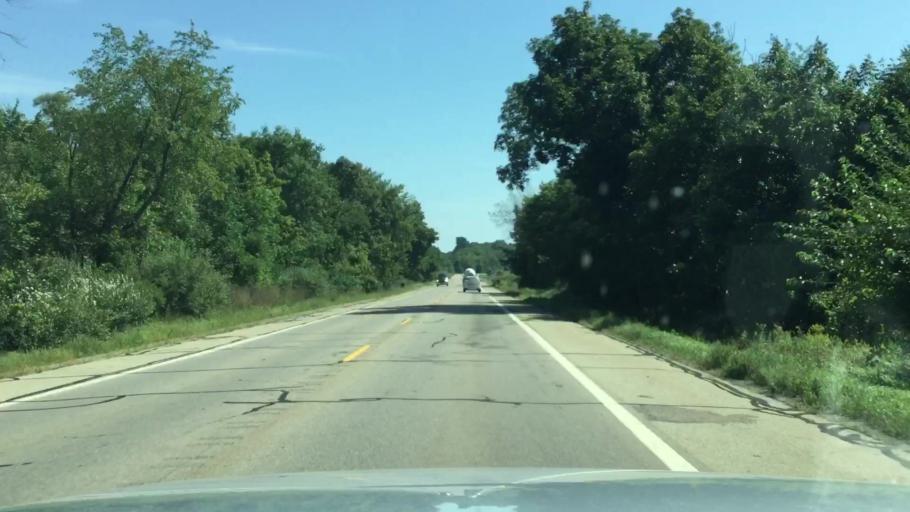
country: US
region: Michigan
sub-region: Lenawee County
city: Clinton
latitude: 42.0732
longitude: -84.0325
